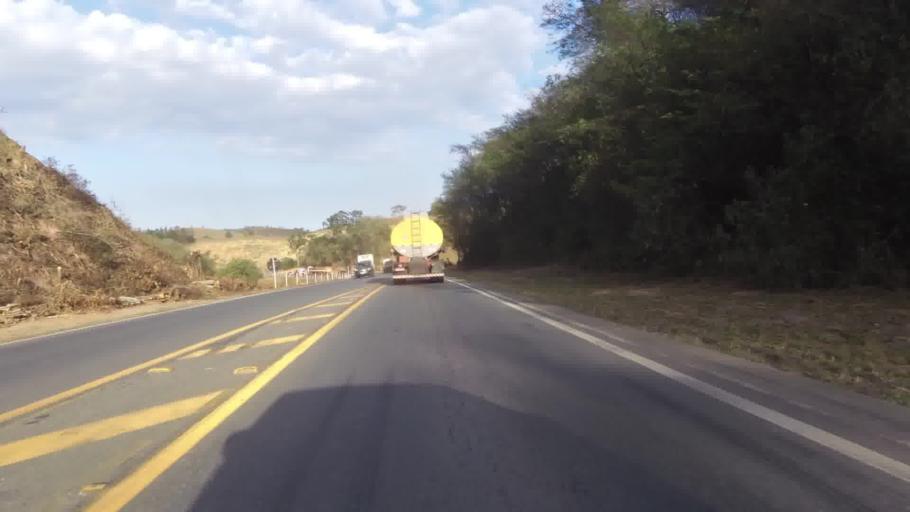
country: BR
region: Espirito Santo
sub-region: Rio Novo Do Sul
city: Rio Novo do Sul
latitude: -20.8998
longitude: -41.0192
